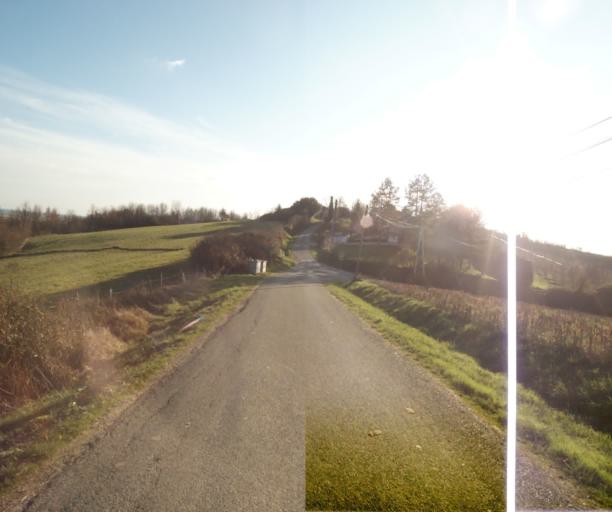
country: FR
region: Midi-Pyrenees
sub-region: Departement du Tarn-et-Garonne
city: Moissac
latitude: 44.1324
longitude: 1.1108
